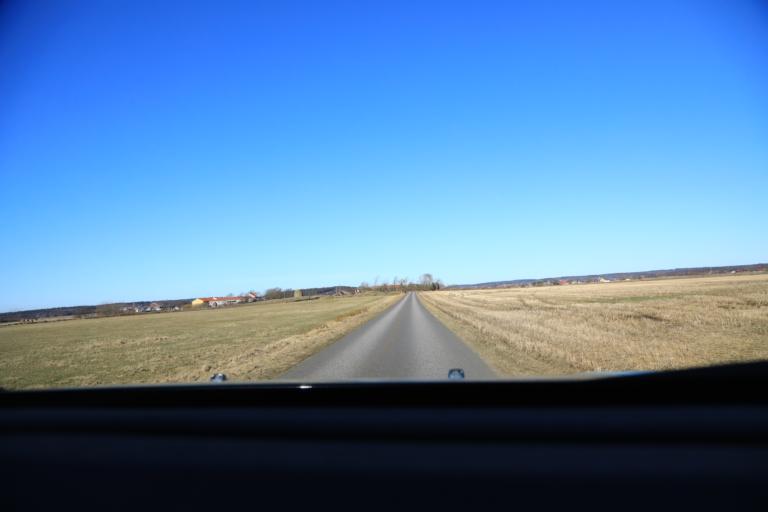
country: SE
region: Halland
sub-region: Kungsbacka Kommun
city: Frillesas
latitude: 57.2283
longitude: 12.1443
